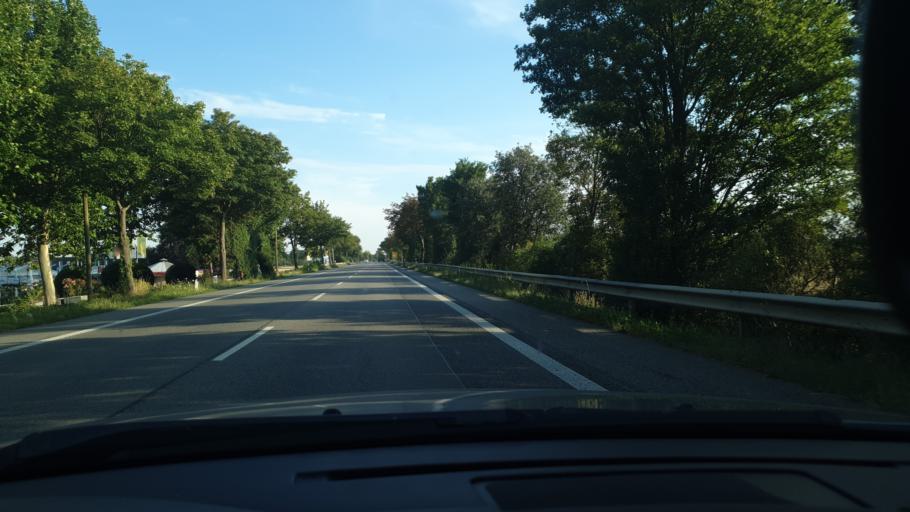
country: DE
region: Rheinland-Pfalz
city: Osthofen
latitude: 49.7184
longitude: 8.3488
